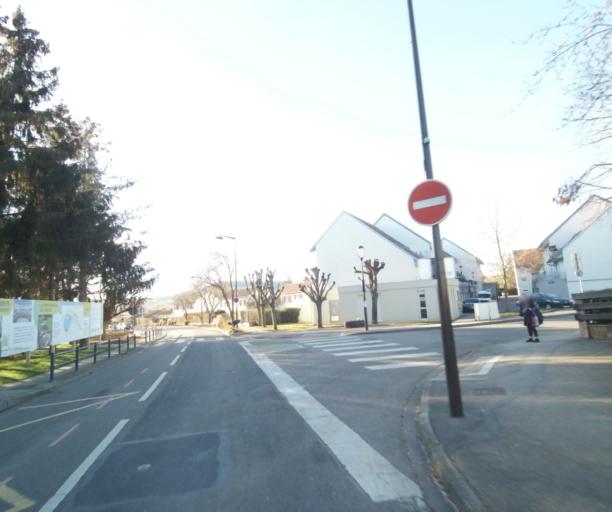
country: FR
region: Lorraine
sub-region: Departement de Meurthe-et-Moselle
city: Seichamps
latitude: 48.7089
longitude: 6.2575
